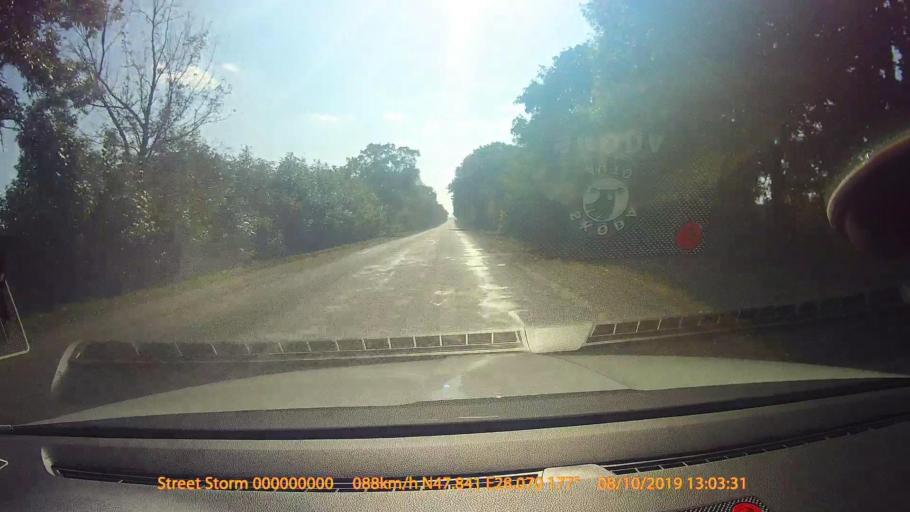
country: MD
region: Singerei
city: Biruinta
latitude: 47.8413
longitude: 28.0698
